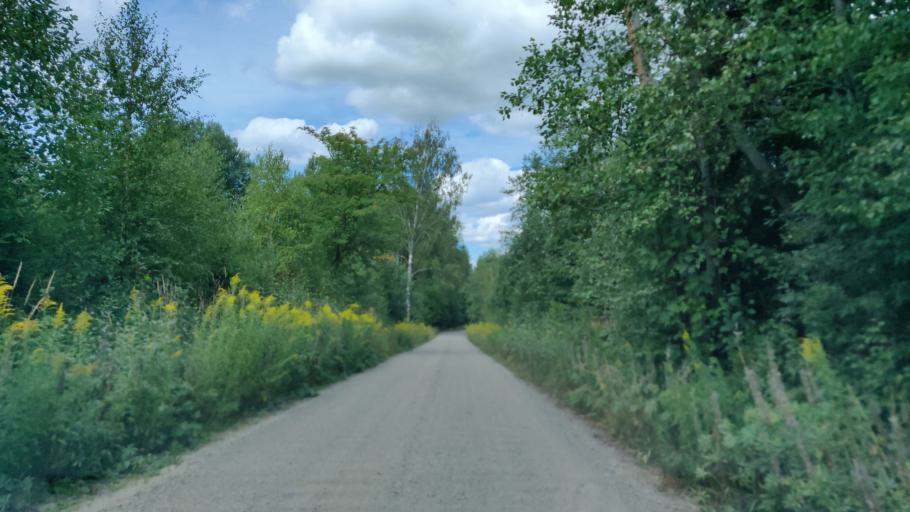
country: SE
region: Vaermland
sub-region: Hagfors Kommun
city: Hagfors
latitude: 60.0163
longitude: 13.6941
